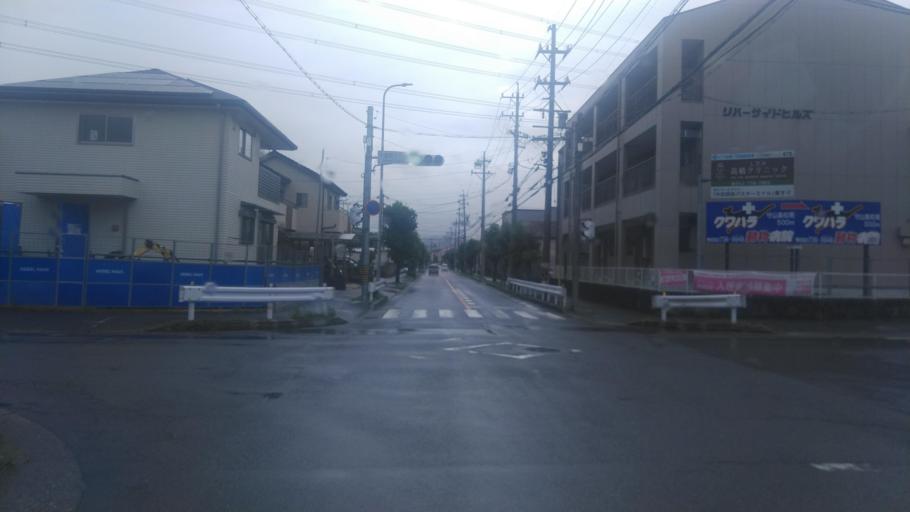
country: JP
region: Aichi
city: Kasugai
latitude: 35.2544
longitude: 137.0188
